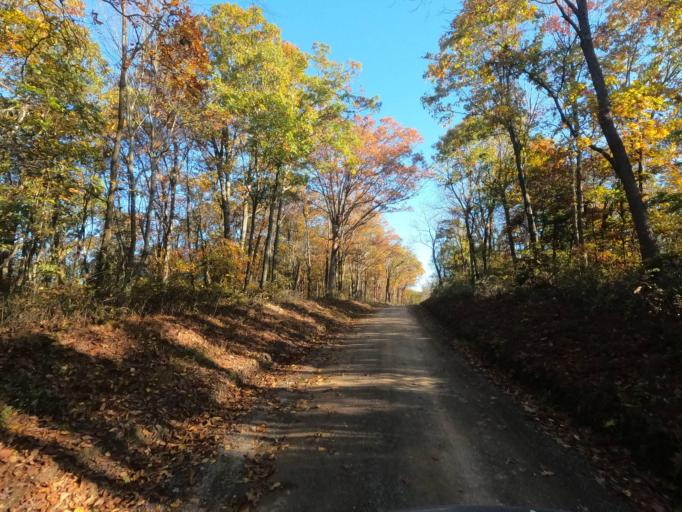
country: US
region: West Virginia
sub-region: Mineral County
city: Fort Ashby
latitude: 39.5601
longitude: -78.5243
